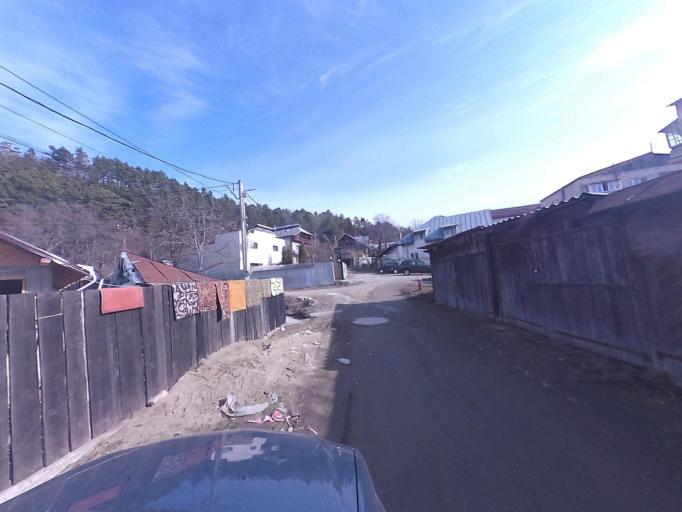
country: RO
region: Neamt
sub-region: Oras Targu Neamt
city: Targu Neamt
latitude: 47.2082
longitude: 26.3605
